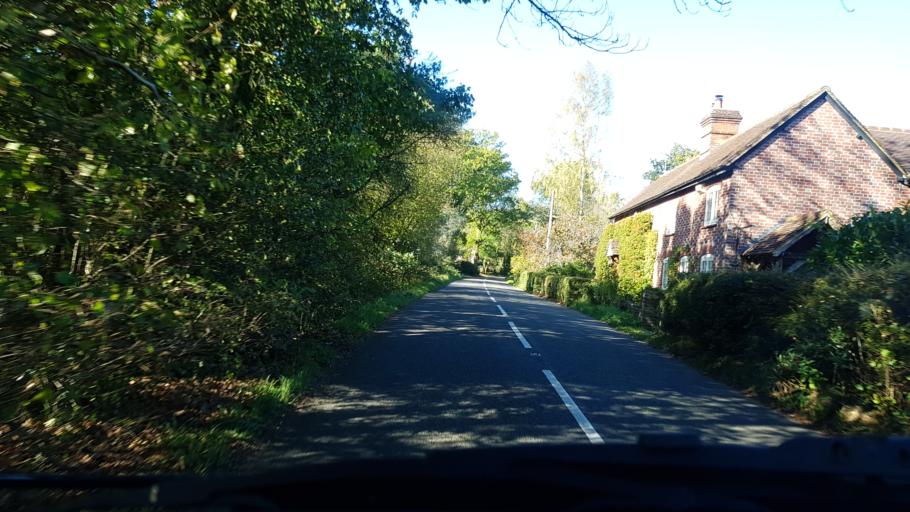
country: GB
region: England
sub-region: Surrey
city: Ockley
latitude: 51.1681
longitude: -0.3993
